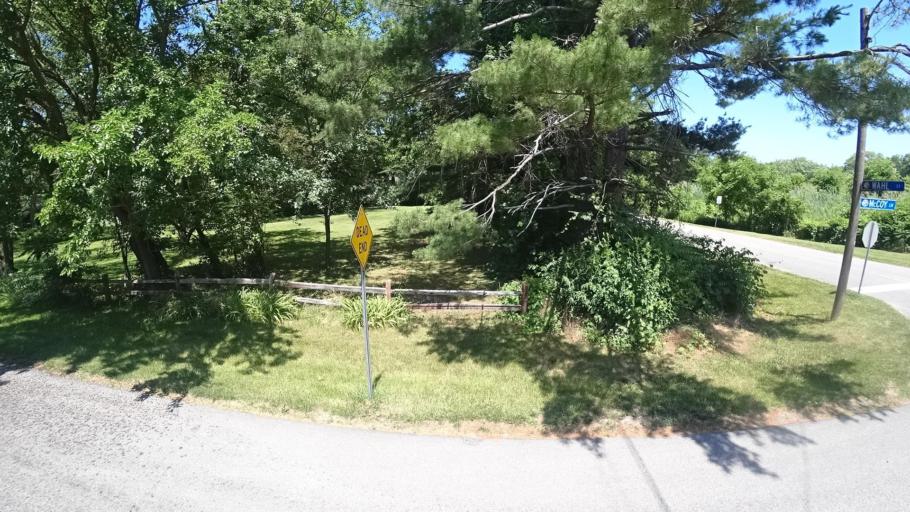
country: US
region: Indiana
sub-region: Porter County
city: Burns Harbor
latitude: 41.6048
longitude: -87.1261
